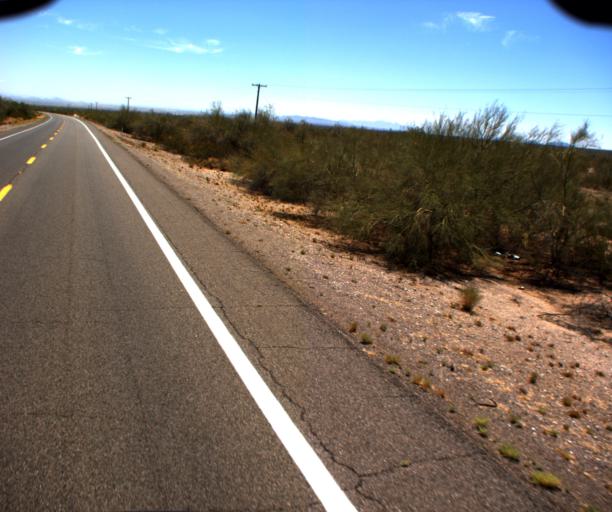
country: US
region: Arizona
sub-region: Pinal County
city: Maricopa
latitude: 32.8419
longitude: -112.1075
